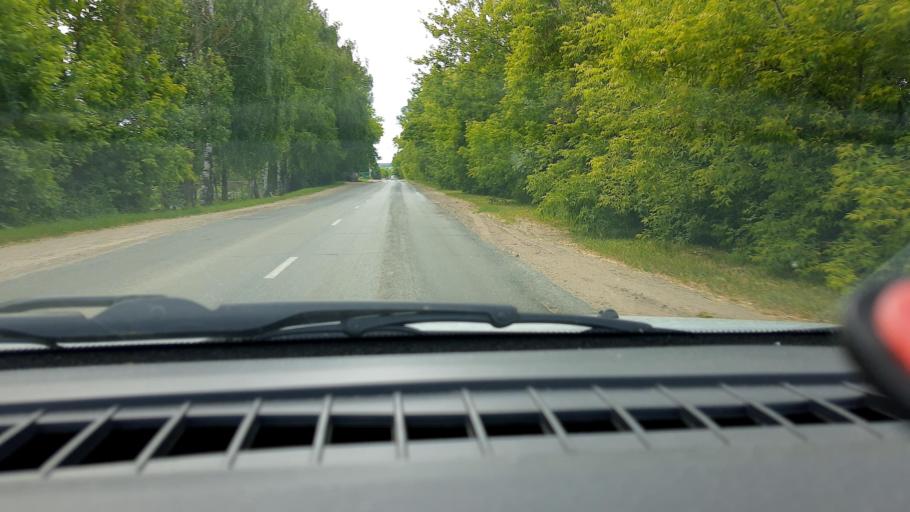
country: RU
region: Nizjnij Novgorod
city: Kstovo
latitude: 56.1335
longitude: 44.0877
